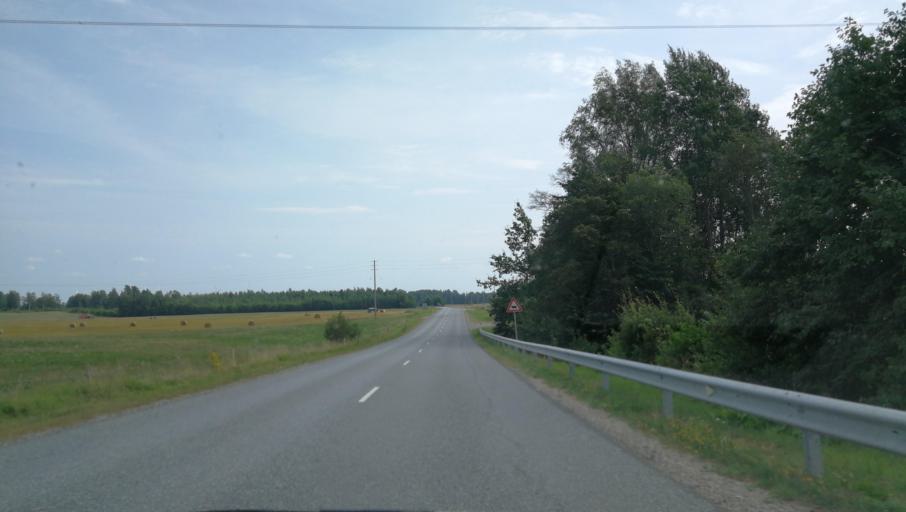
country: LV
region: Alsunga
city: Alsunga
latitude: 56.9889
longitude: 21.5910
